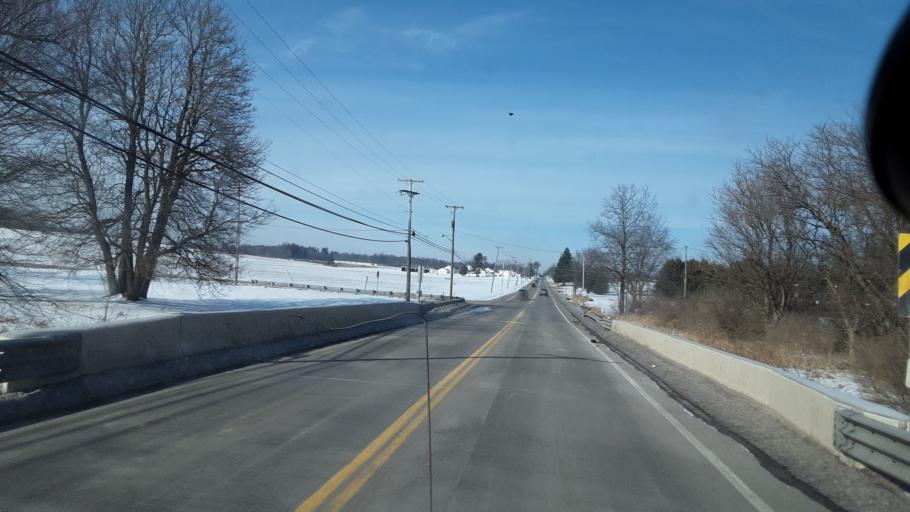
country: US
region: Ohio
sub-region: Mahoning County
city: Canfield
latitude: 41.0023
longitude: -80.7608
